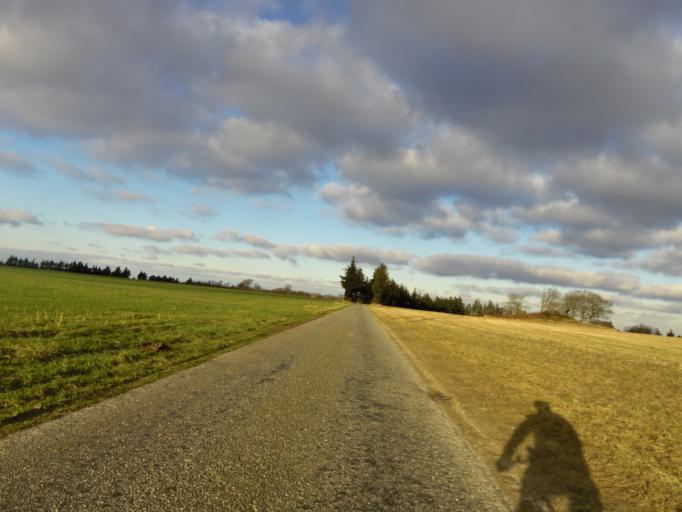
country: DK
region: South Denmark
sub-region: Esbjerg Kommune
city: Ribe
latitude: 55.2683
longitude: 8.8650
